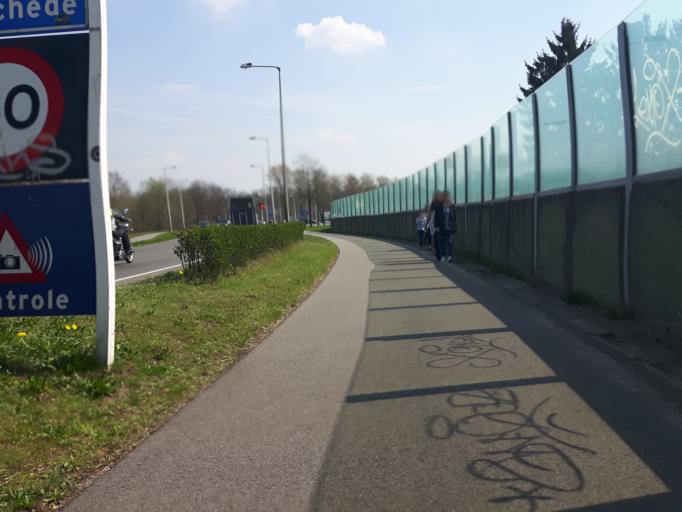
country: NL
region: Overijssel
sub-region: Gemeente Enschede
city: Enschede
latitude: 52.2010
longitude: 6.8600
